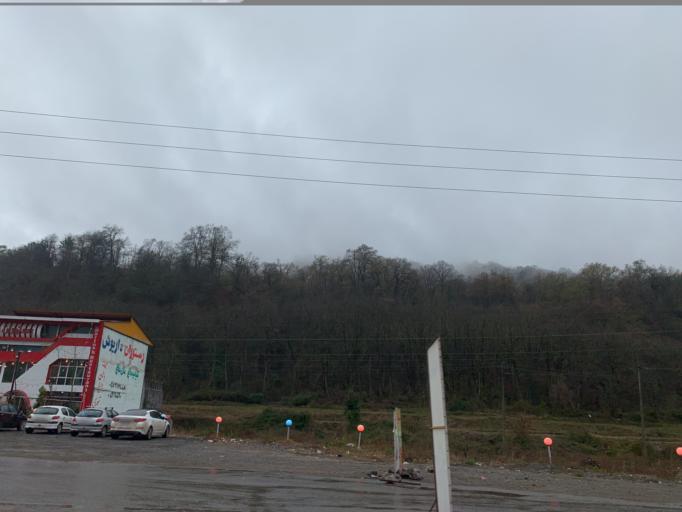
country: IR
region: Mazandaran
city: Amol
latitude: 36.3740
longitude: 52.3528
